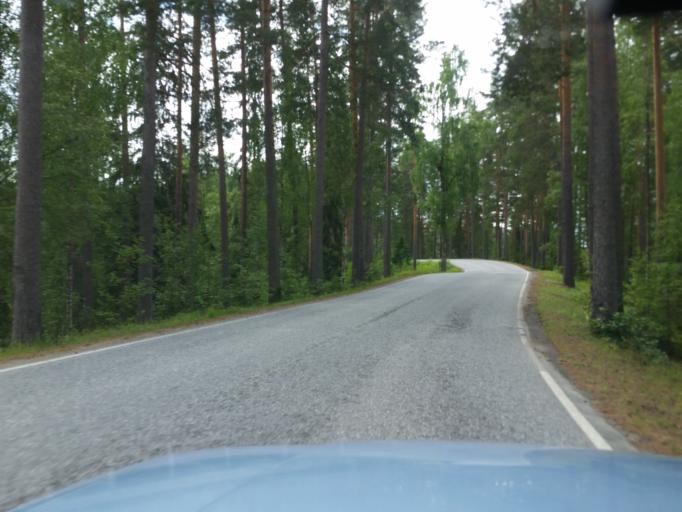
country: FI
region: Southern Savonia
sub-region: Savonlinna
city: Sulkava
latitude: 61.7958
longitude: 28.4182
